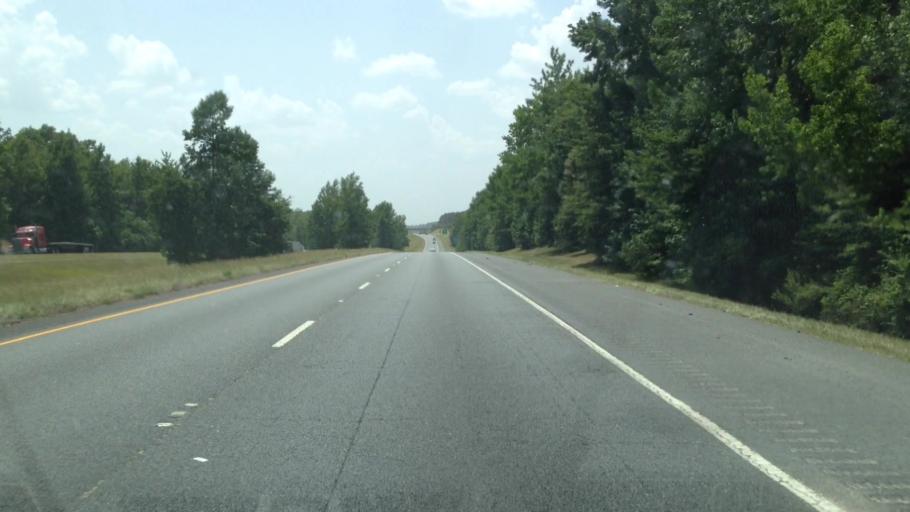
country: US
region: Louisiana
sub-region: Lincoln Parish
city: Grambling
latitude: 32.5458
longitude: -92.7538
